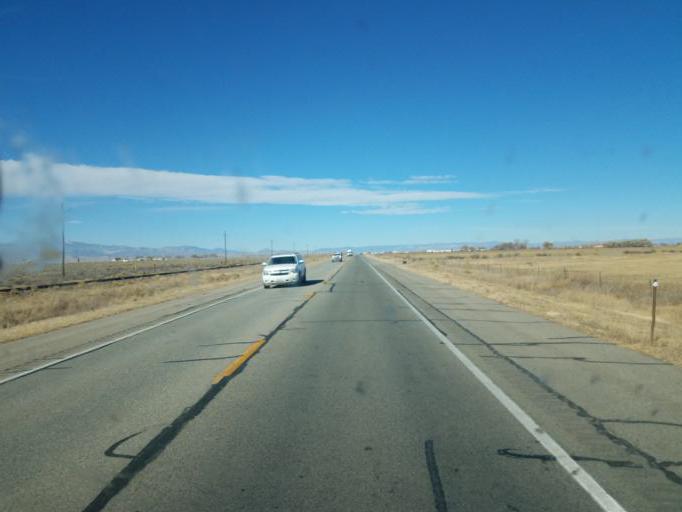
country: US
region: Colorado
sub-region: Alamosa County
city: Alamosa
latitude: 37.5092
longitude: -105.9748
